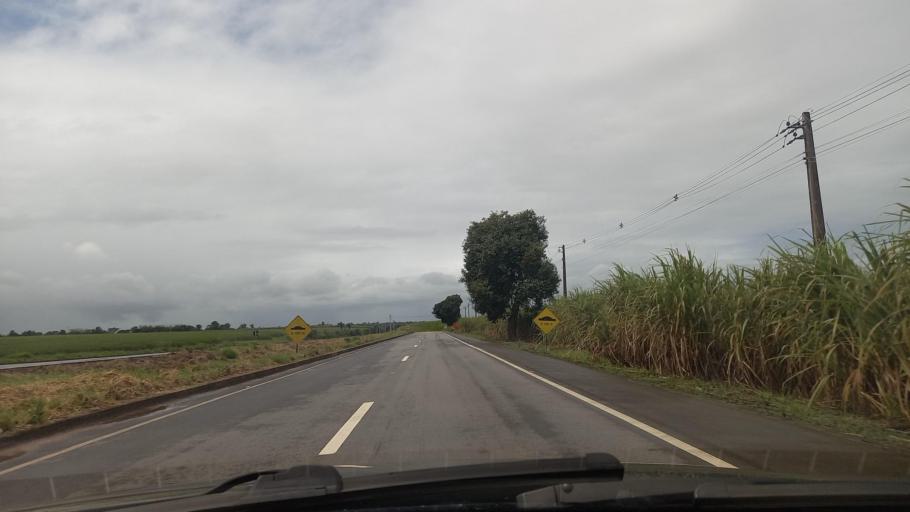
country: BR
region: Alagoas
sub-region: Campo Alegre
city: Campo Alegre
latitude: -9.8230
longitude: -36.2352
